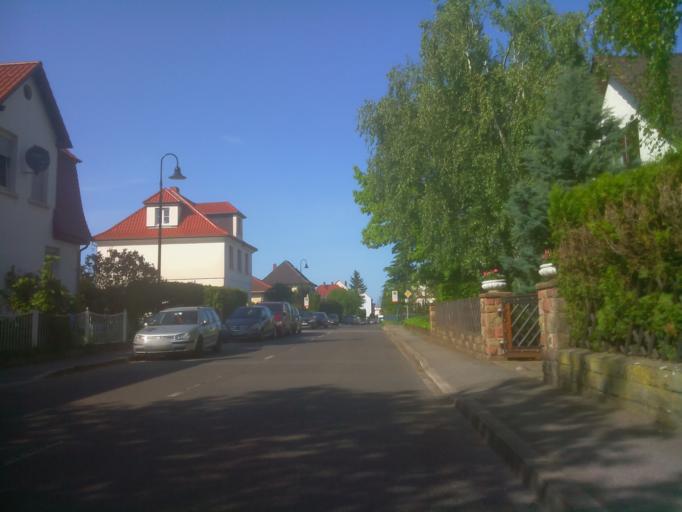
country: DE
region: Baden-Wuerttemberg
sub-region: Karlsruhe Region
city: Edingen-Neckarhausen
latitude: 49.4490
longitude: 8.5850
